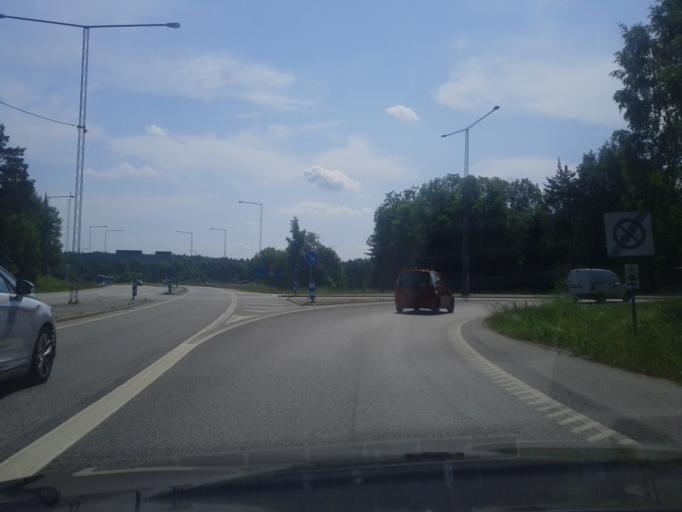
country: SE
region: Stockholm
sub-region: Taby Kommun
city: Taby
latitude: 59.4569
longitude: 18.1335
